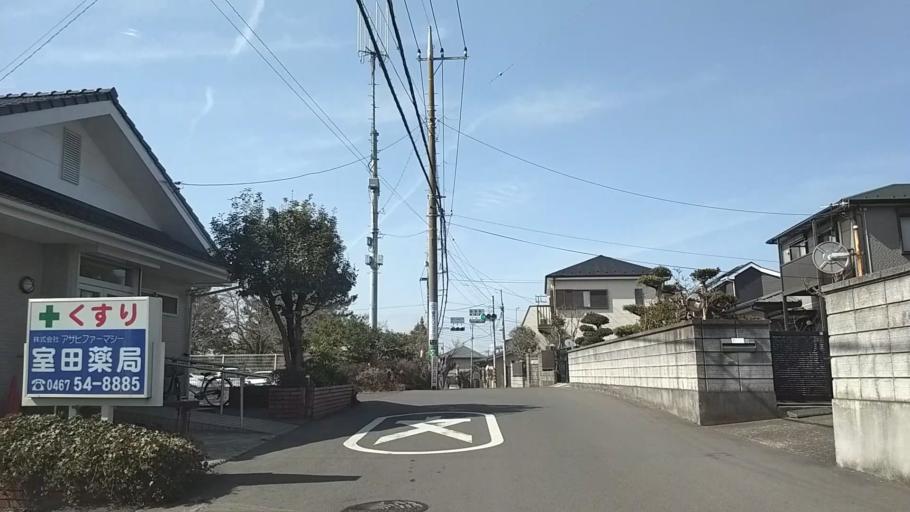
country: JP
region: Kanagawa
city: Chigasaki
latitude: 35.3473
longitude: 139.4216
